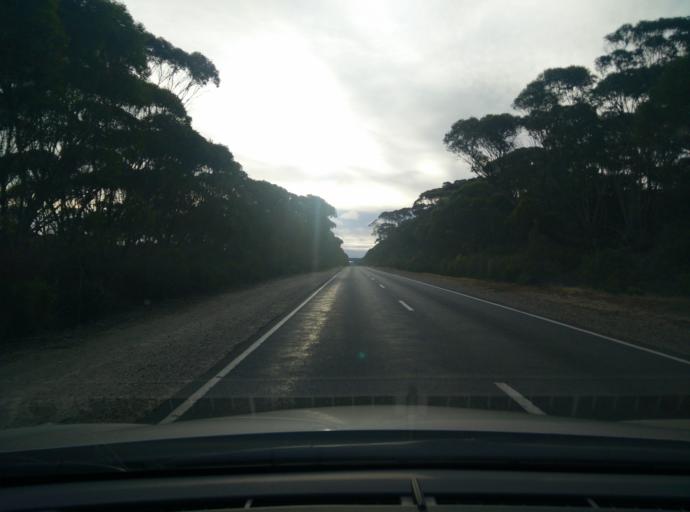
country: AU
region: South Australia
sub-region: Kangaroo Island
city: Kingscote
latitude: -35.7988
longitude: 137.8474
